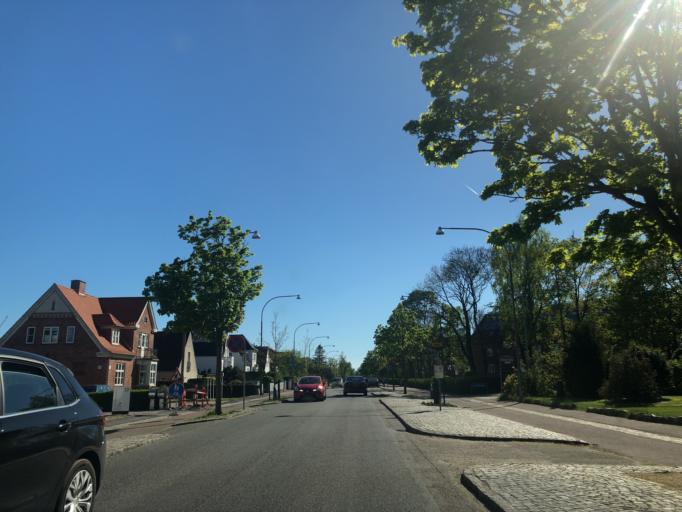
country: DK
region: Zealand
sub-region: Koge Kommune
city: Koge
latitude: 55.4524
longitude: 12.1789
